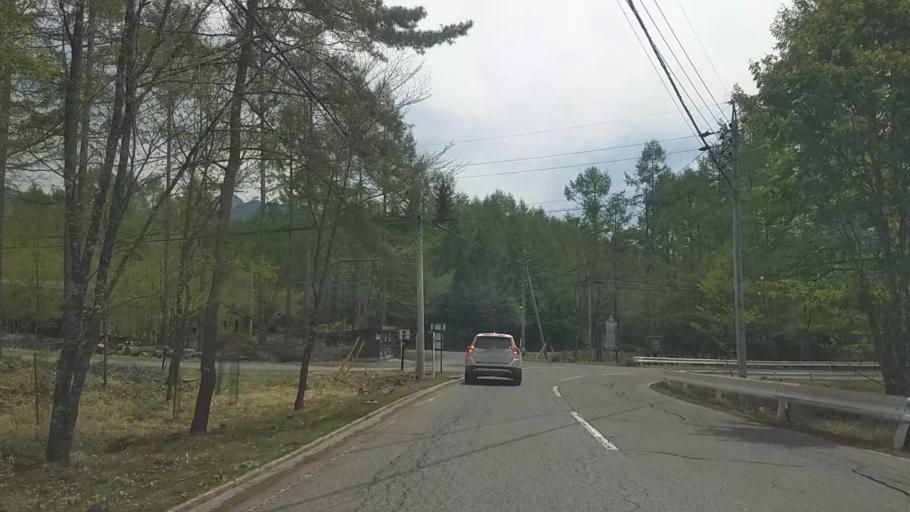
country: JP
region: Nagano
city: Chino
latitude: 36.0455
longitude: 138.2987
